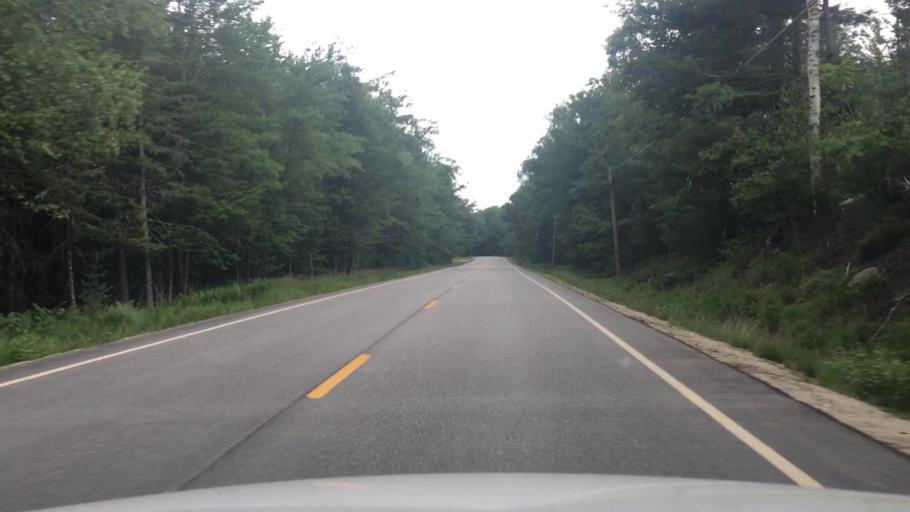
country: US
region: Maine
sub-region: Oxford County
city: Hartford
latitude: 44.3727
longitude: -70.4023
